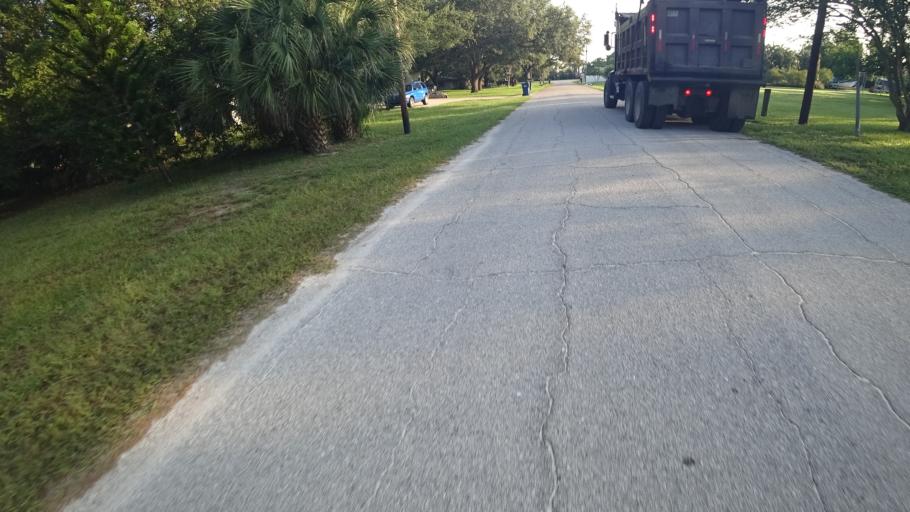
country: US
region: Florida
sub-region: Manatee County
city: West Bradenton
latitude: 27.5200
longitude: -82.6019
